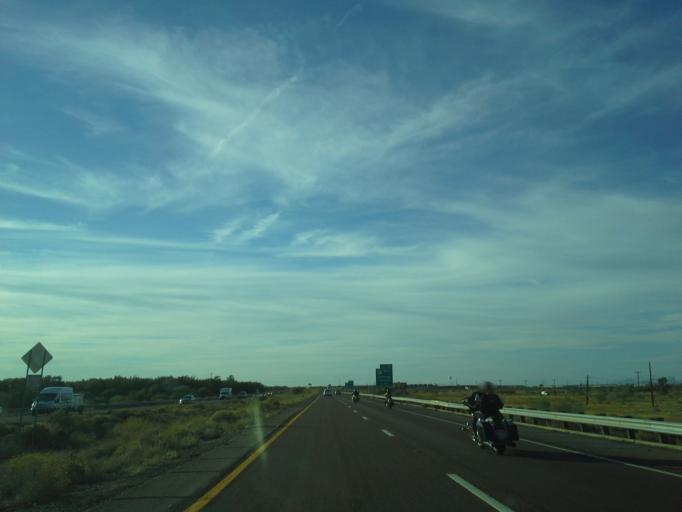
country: US
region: Arizona
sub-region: Pinal County
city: Eloy
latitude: 32.7159
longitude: -111.5039
